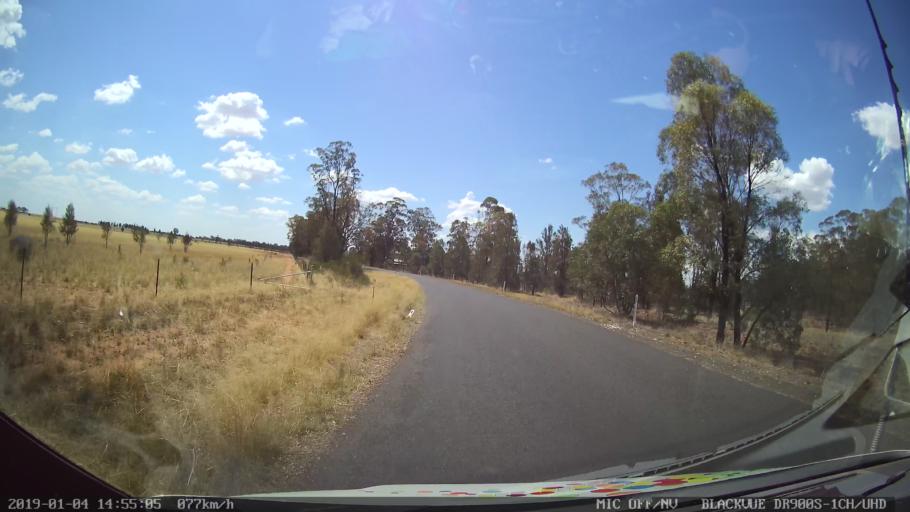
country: AU
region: New South Wales
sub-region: Dubbo Municipality
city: Dubbo
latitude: -31.9831
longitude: 148.6547
